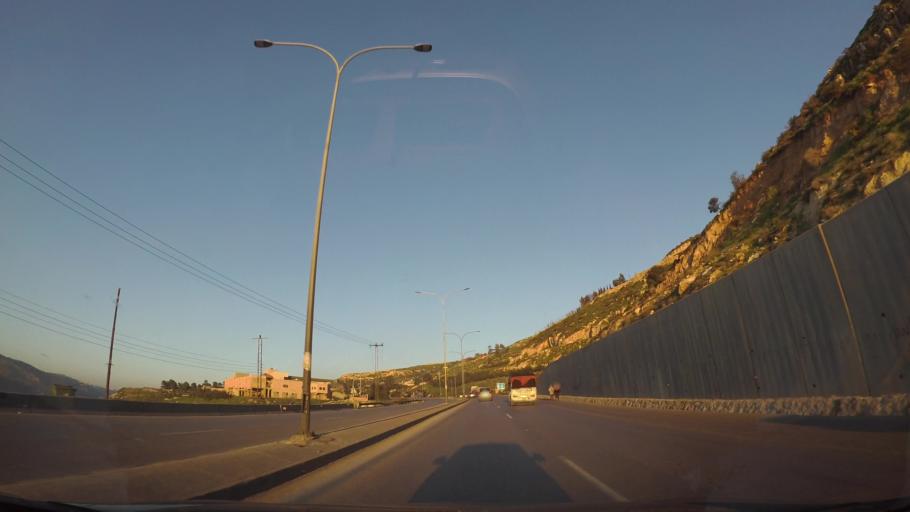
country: JO
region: Amman
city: Umm as Summaq
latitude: 31.8743
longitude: 35.7753
